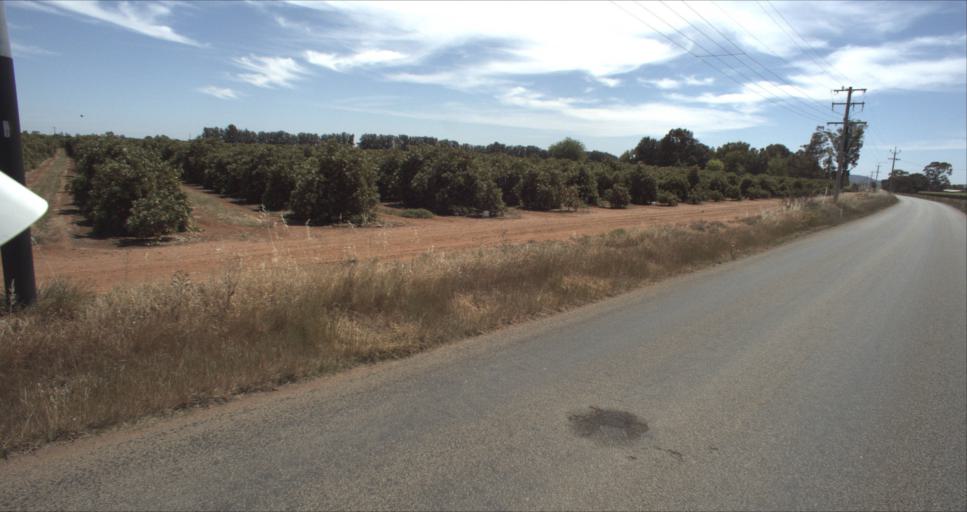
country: AU
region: New South Wales
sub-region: Leeton
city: Leeton
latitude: -34.5641
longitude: 146.4521
